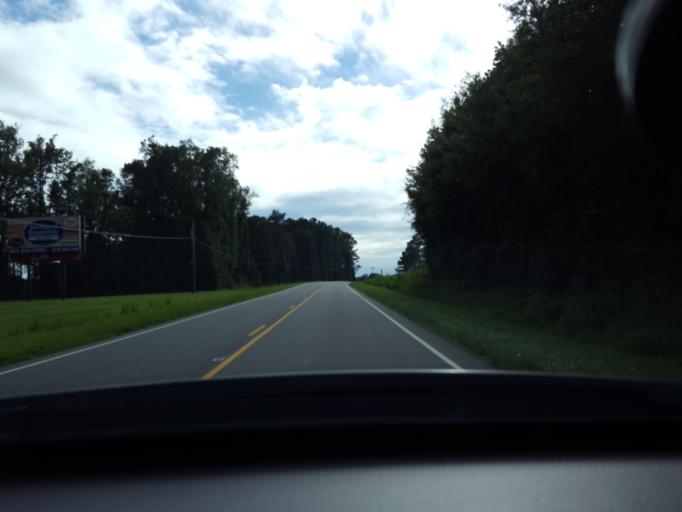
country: US
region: North Carolina
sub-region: Duplin County
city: Kenansville
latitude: 35.0151
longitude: -77.8707
